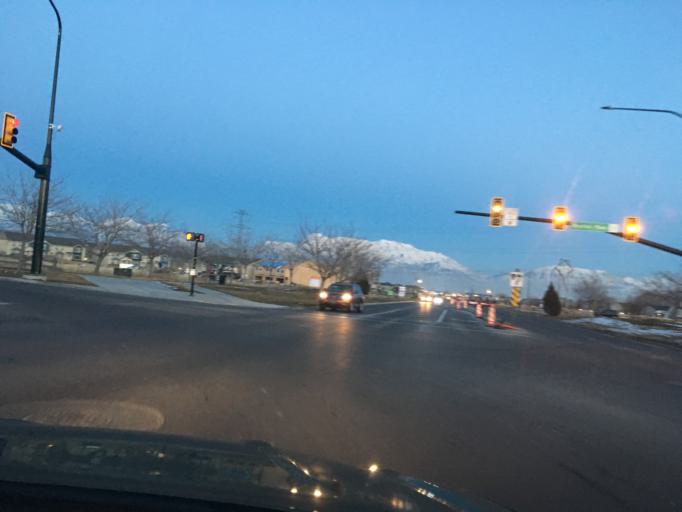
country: US
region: Utah
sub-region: Utah County
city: Eagle Mountain
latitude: 40.3622
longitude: -111.9766
